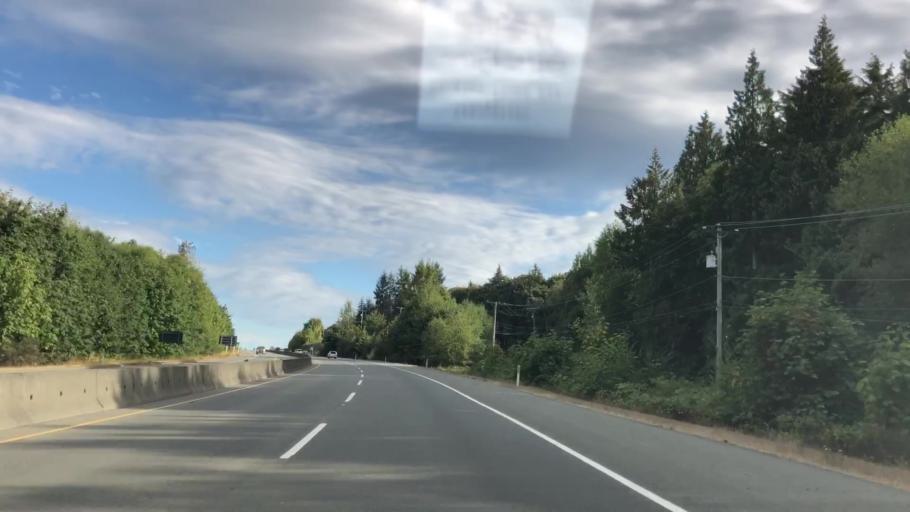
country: CA
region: British Columbia
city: North Saanich
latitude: 48.6487
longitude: -123.5592
